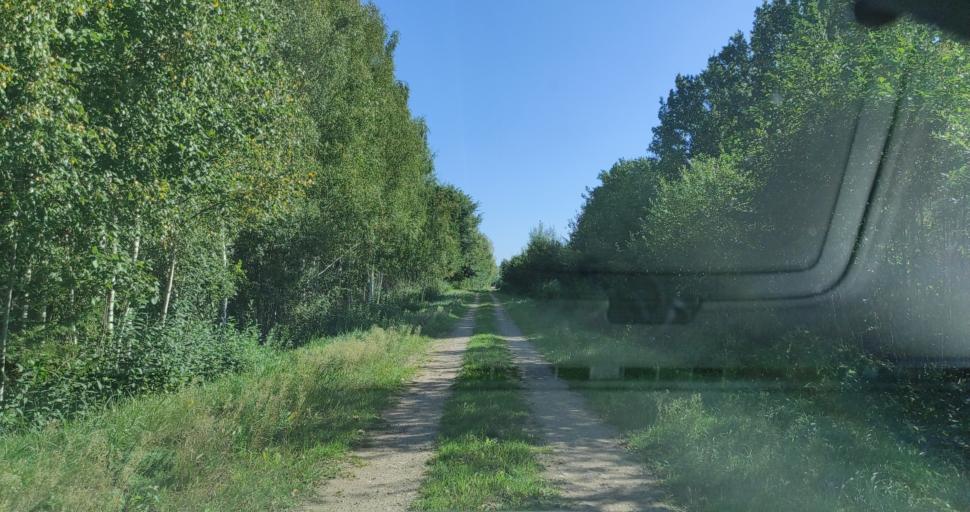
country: LV
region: Kuldigas Rajons
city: Kuldiga
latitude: 56.9749
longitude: 21.9194
